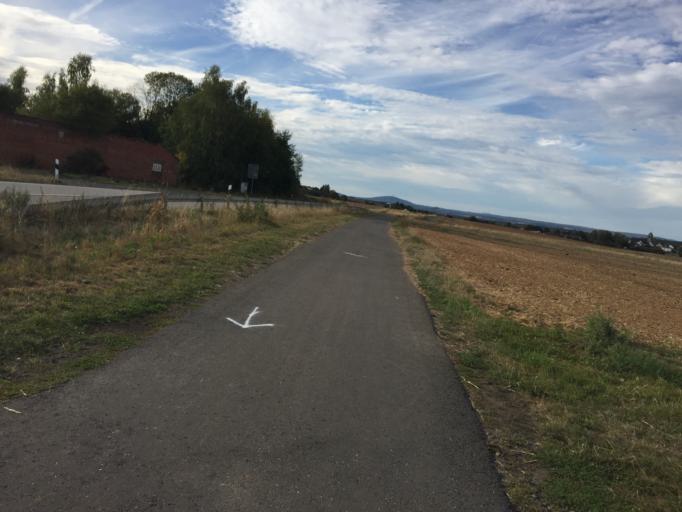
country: DE
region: Hesse
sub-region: Regierungsbezirk Giessen
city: Langgons
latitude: 50.5236
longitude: 8.7190
